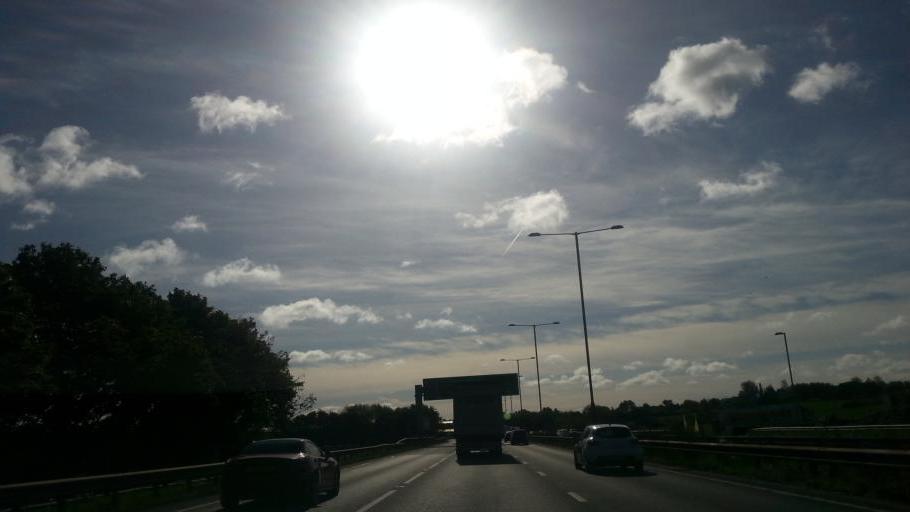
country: GB
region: England
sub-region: Northamptonshire
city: Kettering
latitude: 52.3812
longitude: -0.7298
